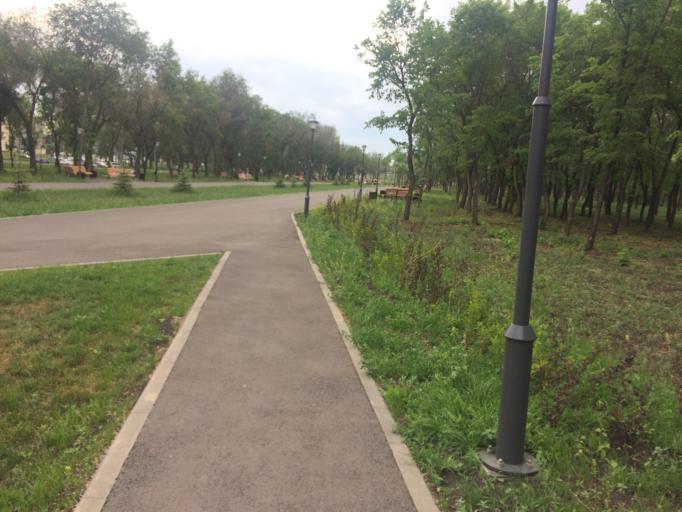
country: RU
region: Chelyabinsk
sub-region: Gorod Magnitogorsk
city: Magnitogorsk
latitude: 53.4022
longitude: 58.9926
